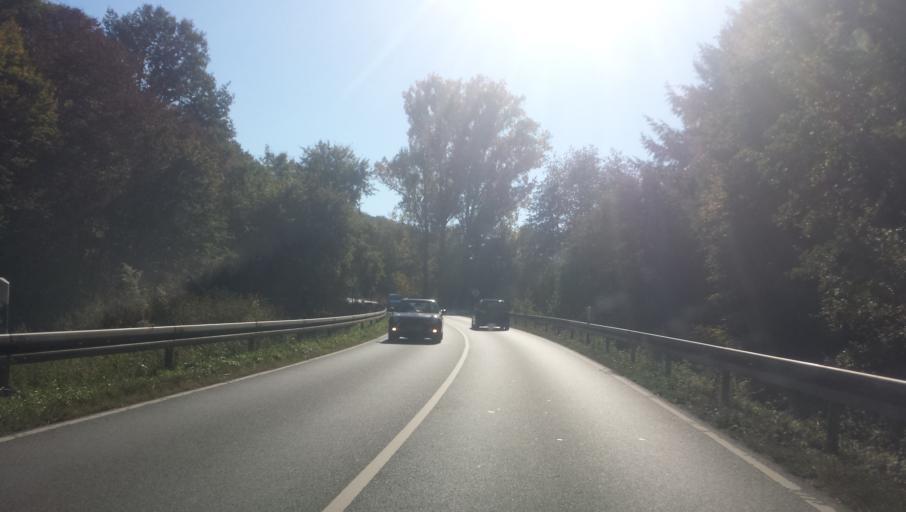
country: DE
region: Hesse
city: Gross-Bieberau
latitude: 49.8103
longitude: 8.7869
